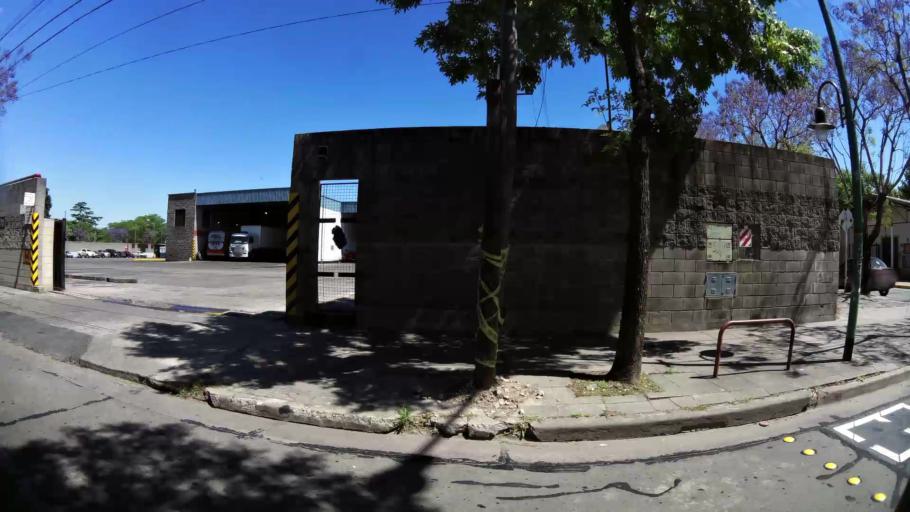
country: AR
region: Buenos Aires
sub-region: Partido de General San Martin
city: General San Martin
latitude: -34.5318
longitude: -58.5440
